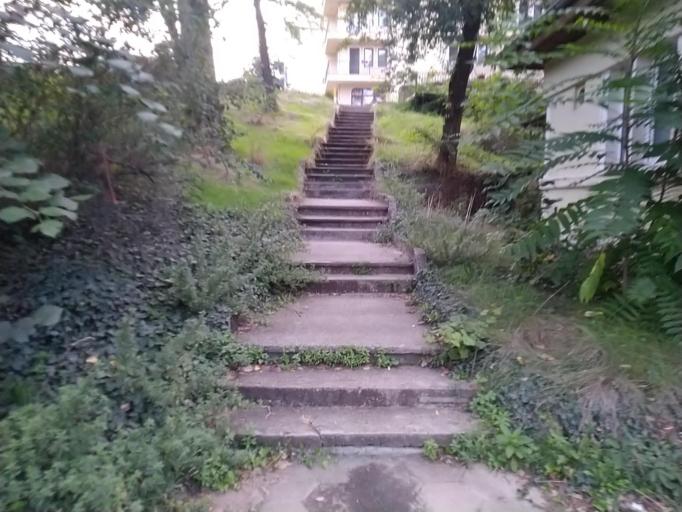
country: BG
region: Plovdiv
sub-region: Obshtina Khisarya
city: Khisarya
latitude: 42.5005
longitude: 24.7027
